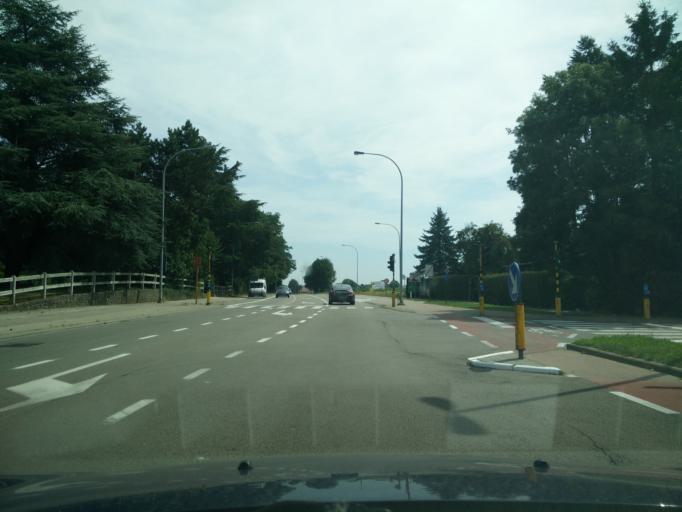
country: BE
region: Flanders
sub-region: Provincie Oost-Vlaanderen
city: Ninove
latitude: 50.8238
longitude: 4.0407
